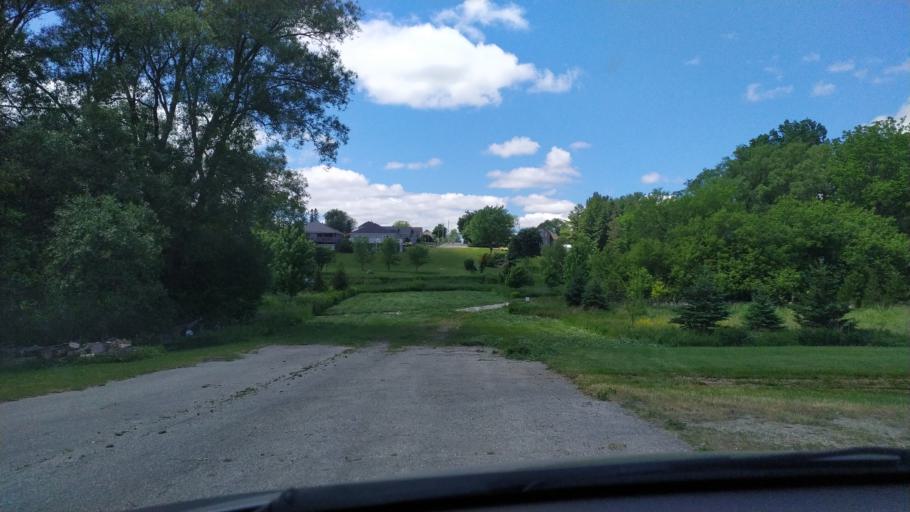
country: CA
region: Ontario
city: Huron East
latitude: 43.4614
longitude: -81.2009
